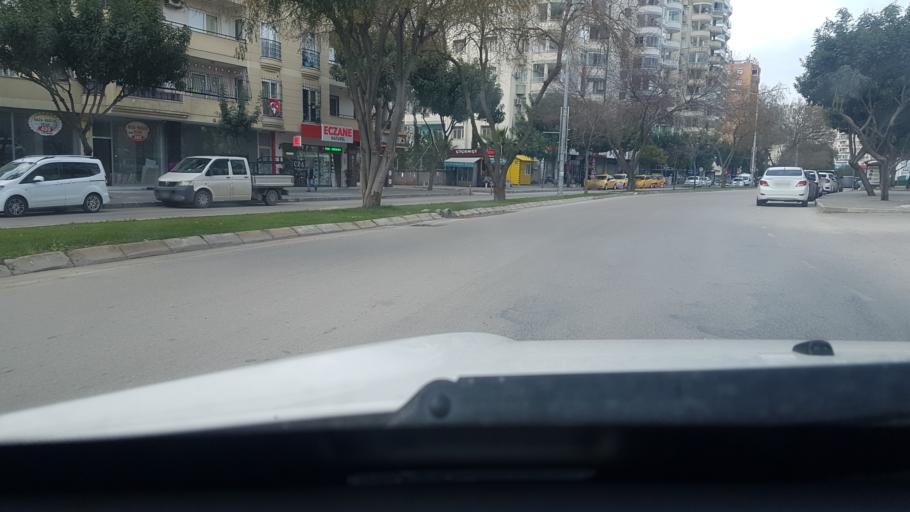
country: TR
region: Adana
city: Adana
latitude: 37.0358
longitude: 35.2977
